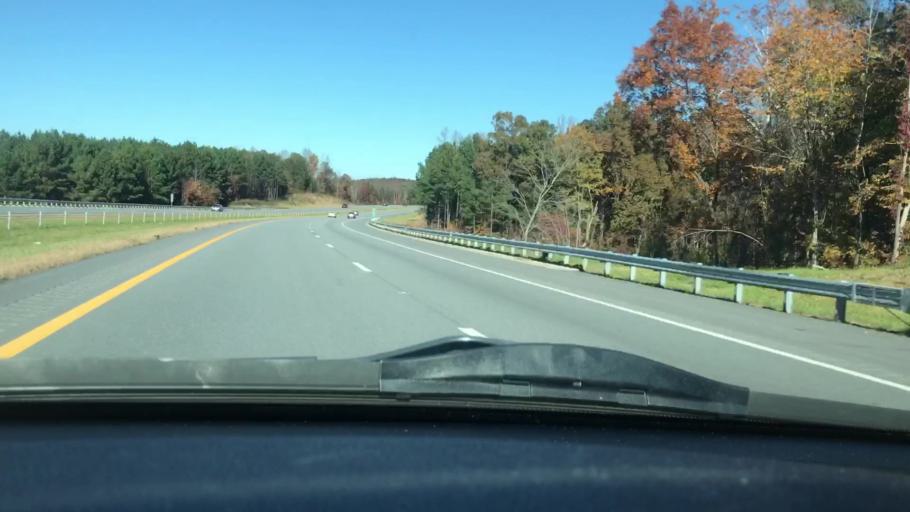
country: US
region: North Carolina
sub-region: Guilford County
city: Oak Ridge
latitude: 36.1606
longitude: -79.9582
